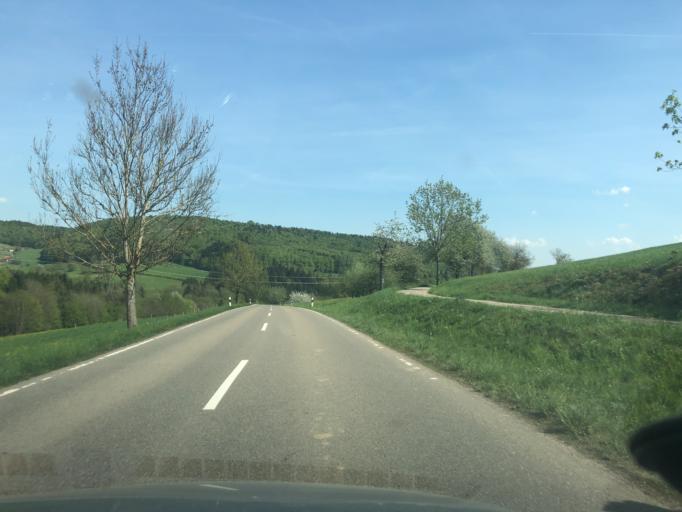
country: DE
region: Baden-Wuerttemberg
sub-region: Freiburg Region
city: Weilheim
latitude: 47.6524
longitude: 8.2389
